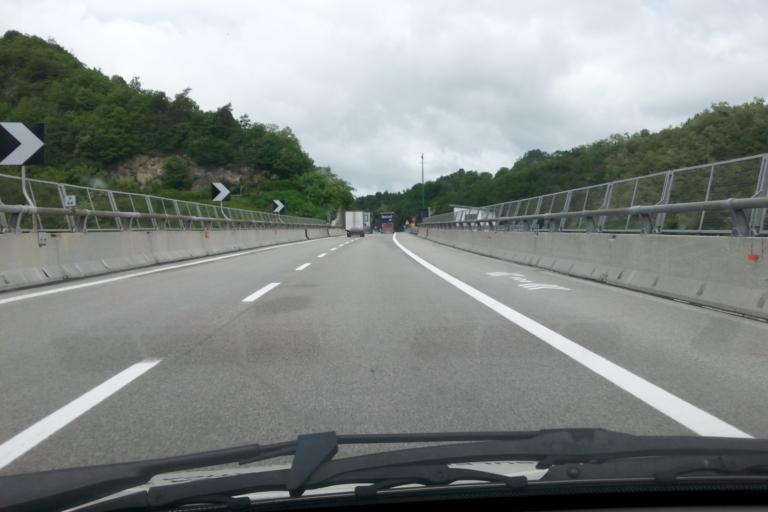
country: IT
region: Liguria
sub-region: Provincia di Savona
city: Valzemola
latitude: 44.3576
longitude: 8.1714
